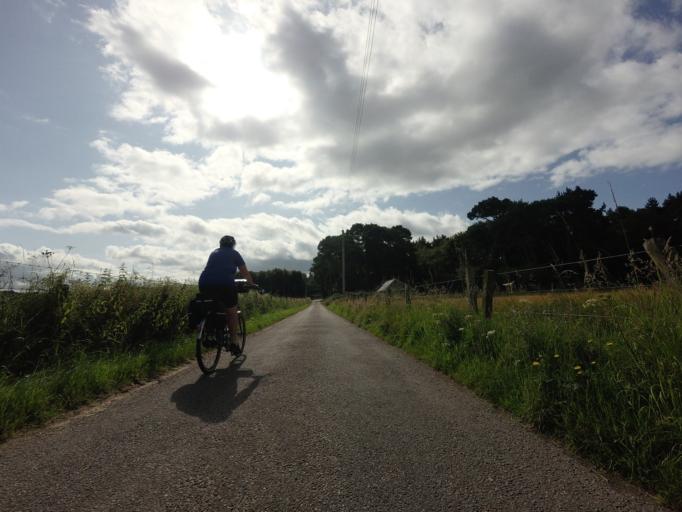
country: GB
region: Scotland
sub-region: Highland
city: Nairn
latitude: 57.5692
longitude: -3.8678
